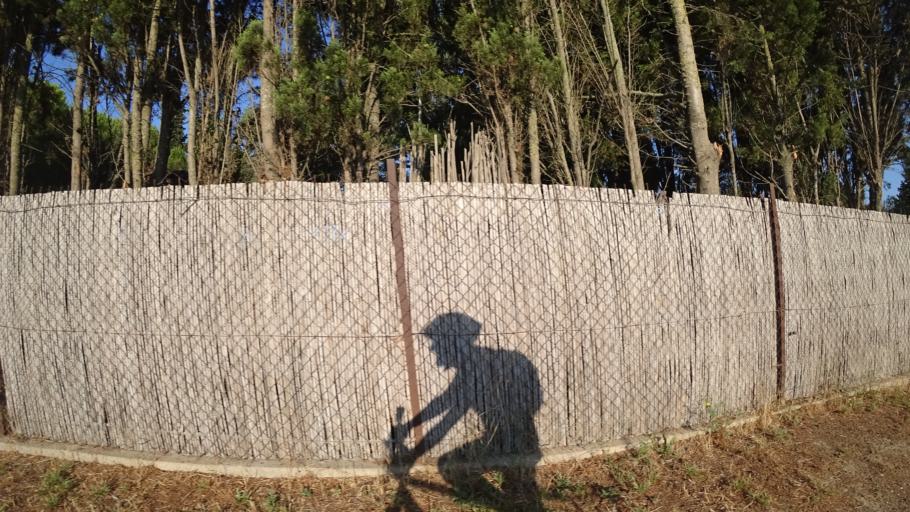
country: FR
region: Languedoc-Roussillon
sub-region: Departement des Pyrenees-Orientales
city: Sainte-Marie-Plage
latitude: 42.7256
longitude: 3.0293
